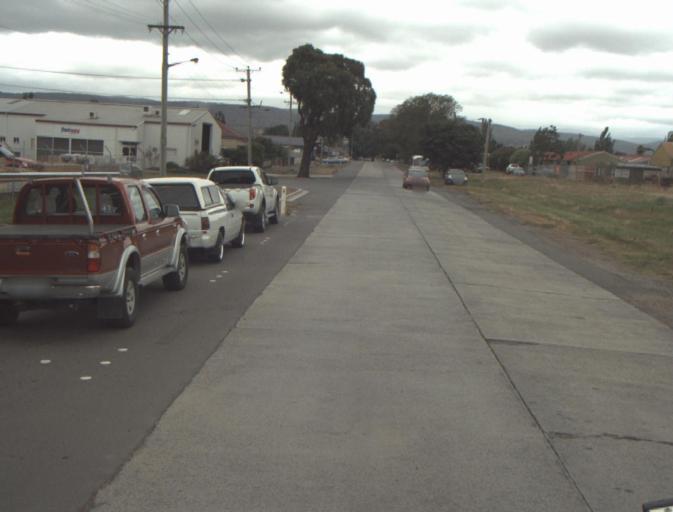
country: AU
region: Tasmania
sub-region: Launceston
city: Launceston
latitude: -41.4282
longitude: 147.1285
